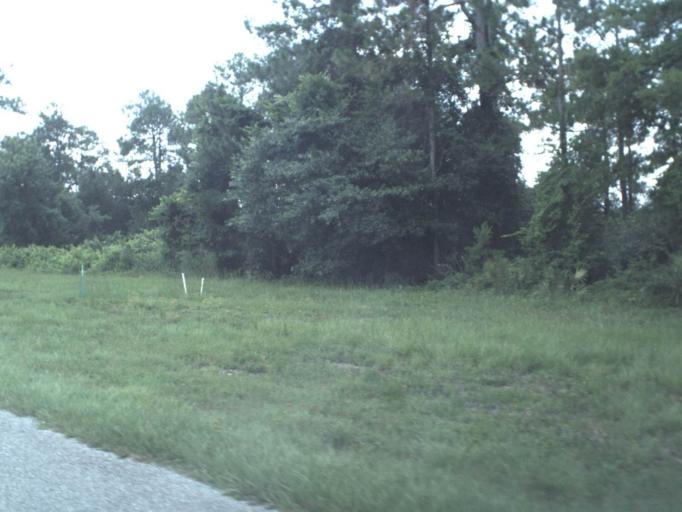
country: US
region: Florida
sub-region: Saint Johns County
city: Palm Valley
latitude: 30.0896
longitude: -81.4637
